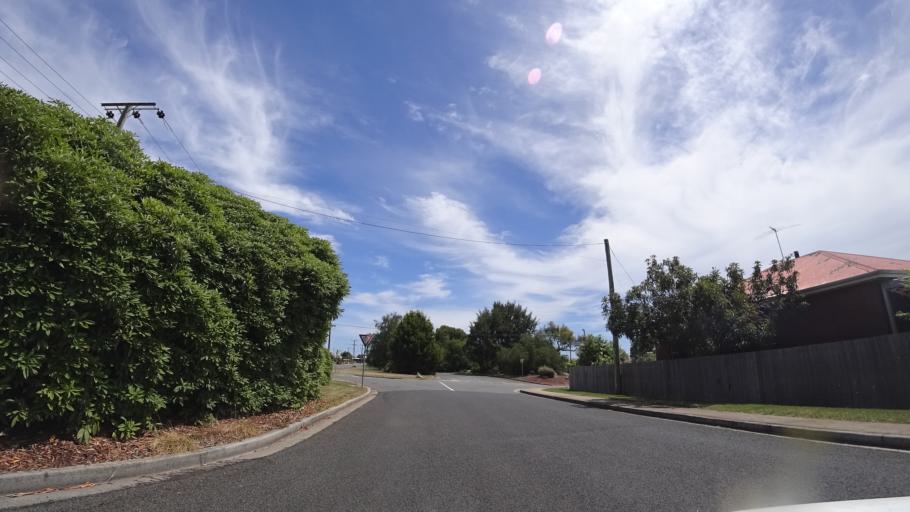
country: AU
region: Tasmania
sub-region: Dorset
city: Scottsdale
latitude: -41.1609
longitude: 147.5130
